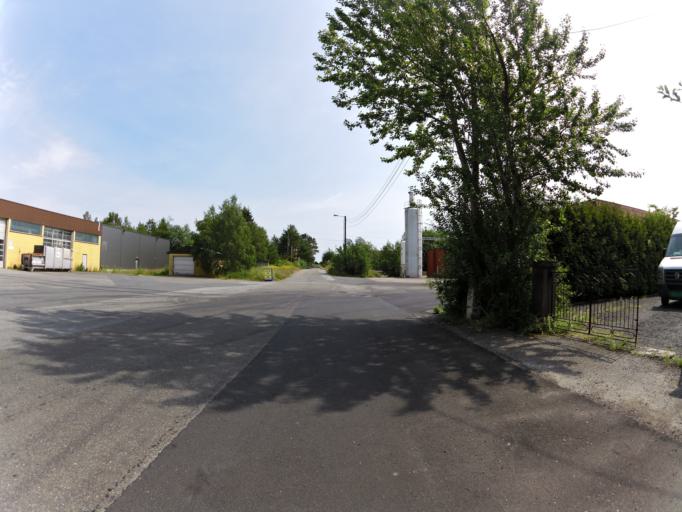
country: NO
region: Ostfold
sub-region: Fredrikstad
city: Fredrikstad
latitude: 59.2456
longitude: 10.9887
